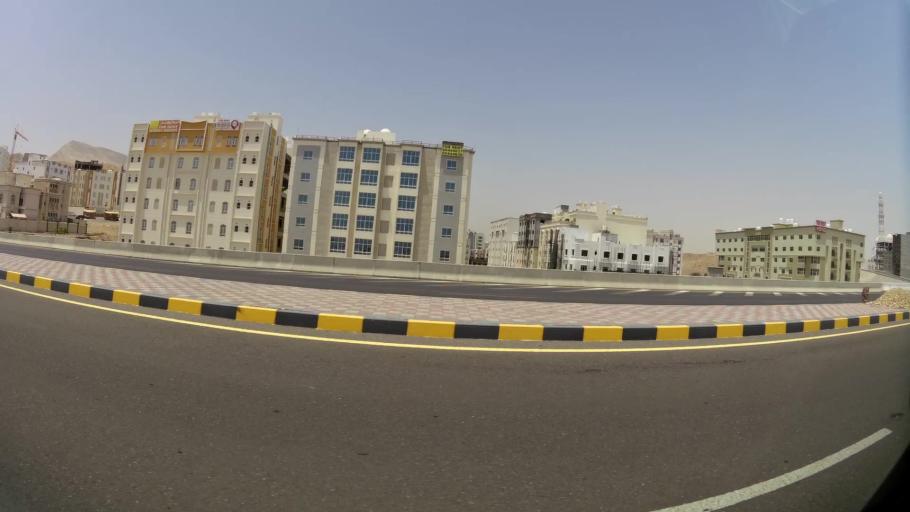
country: OM
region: Muhafazat Masqat
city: Bawshar
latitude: 23.5780
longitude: 58.4199
